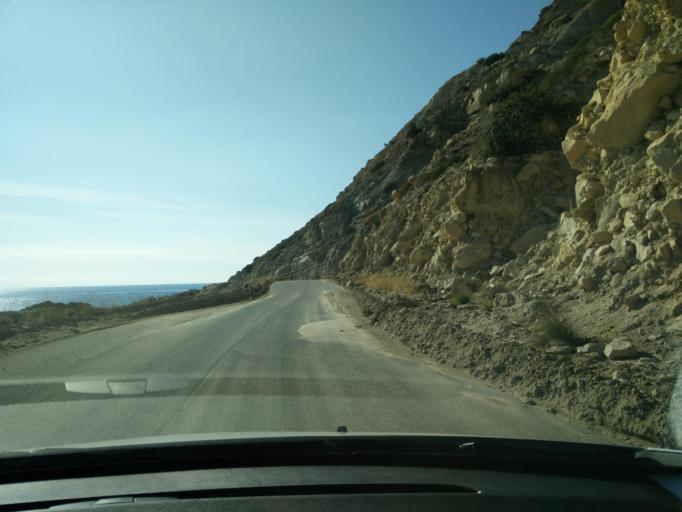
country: GR
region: Crete
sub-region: Nomos Lasithiou
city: Gra Liyia
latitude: 34.9914
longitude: 25.5504
